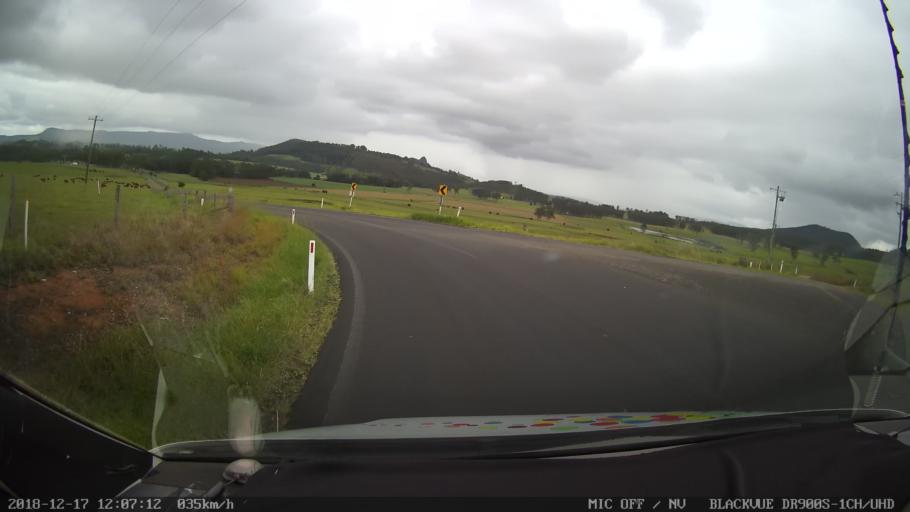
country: AU
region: New South Wales
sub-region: Kyogle
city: Kyogle
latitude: -28.4755
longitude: 152.5671
